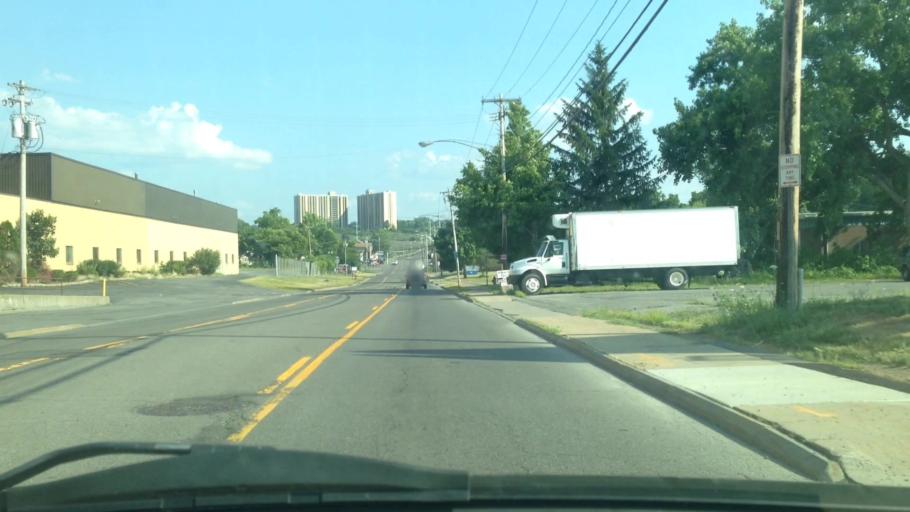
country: US
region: New York
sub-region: Onondaga County
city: Syracuse
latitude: 43.0155
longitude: -76.1365
